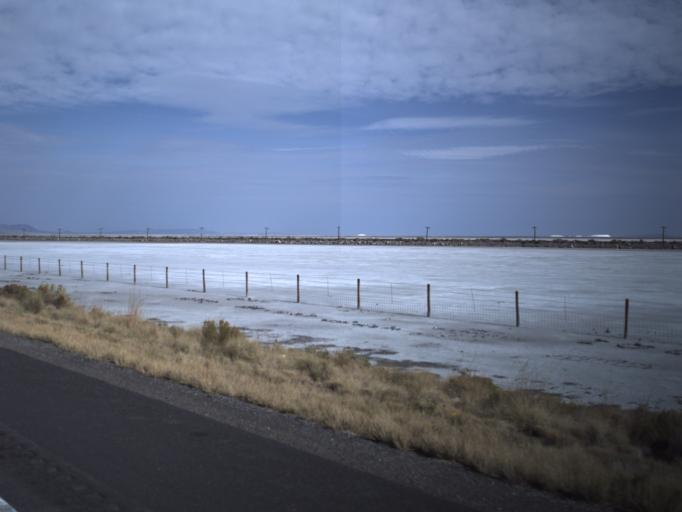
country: US
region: Utah
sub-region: Tooele County
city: Grantsville
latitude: 40.7148
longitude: -112.5410
